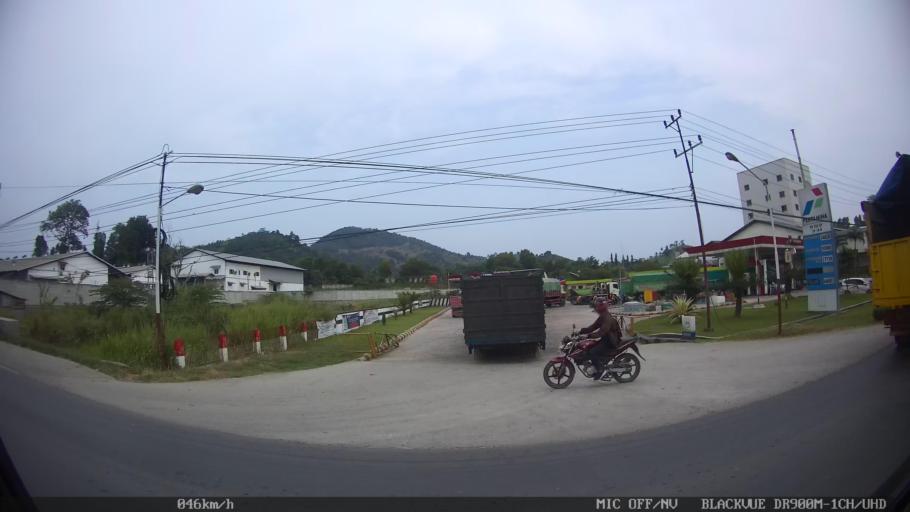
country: ID
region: Lampung
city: Panjang
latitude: -5.4172
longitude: 105.3433
